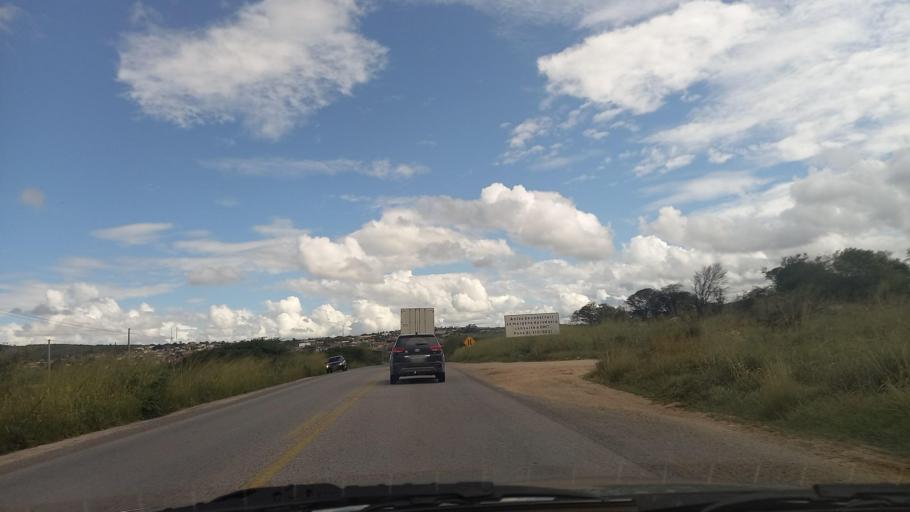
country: BR
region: Pernambuco
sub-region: Lajedo
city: Lajedo
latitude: -8.6947
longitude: -36.4127
